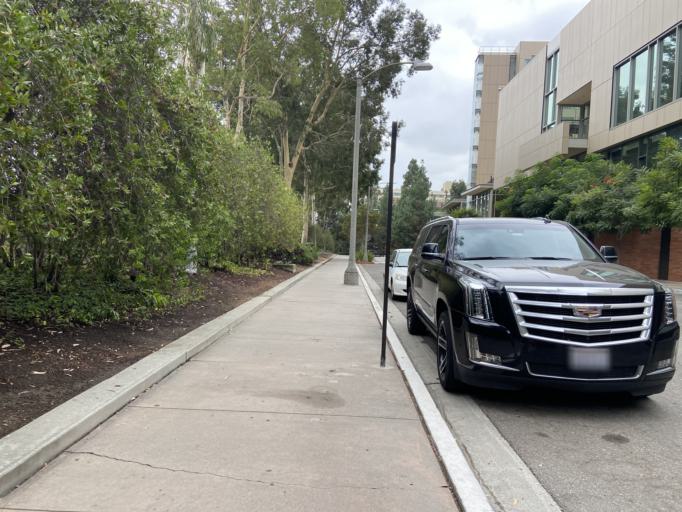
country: US
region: California
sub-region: Los Angeles County
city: Westwood, Los Angeles
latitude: 34.0724
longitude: -118.4496
